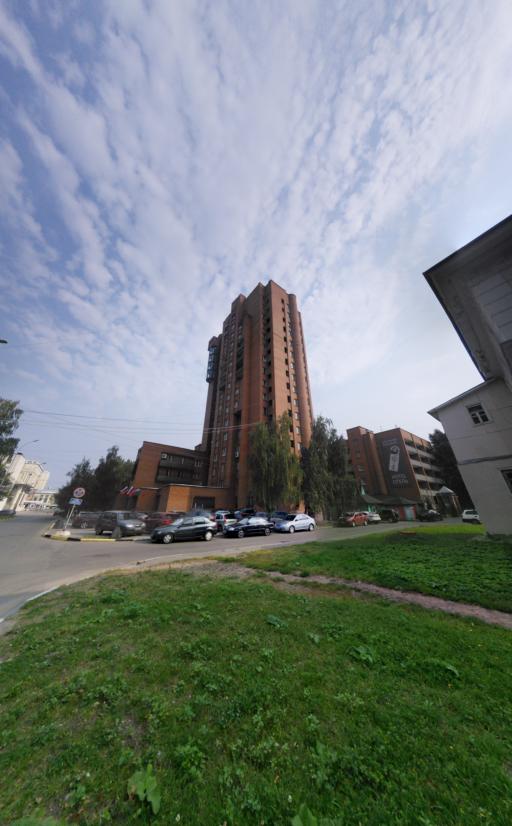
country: RU
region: Jaroslavl
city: Yaroslavl
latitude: 57.6233
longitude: 39.8772
